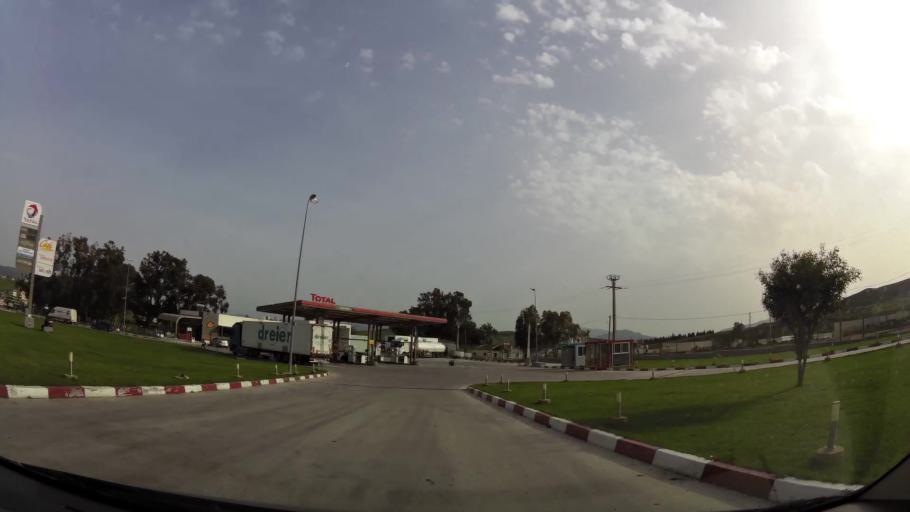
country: MA
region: Tanger-Tetouan
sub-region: Tanger-Assilah
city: Dar Chaoui
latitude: 35.6559
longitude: -5.6906
